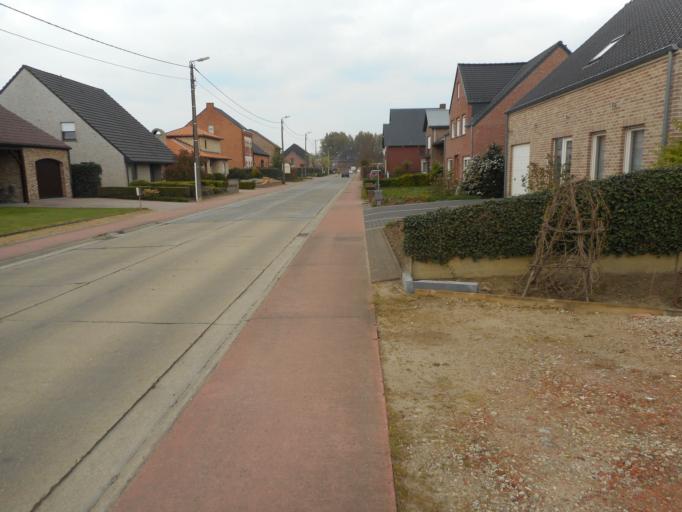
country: BE
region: Flanders
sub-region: Provincie Vlaams-Brabant
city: Begijnendijk
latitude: 51.0126
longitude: 4.7880
